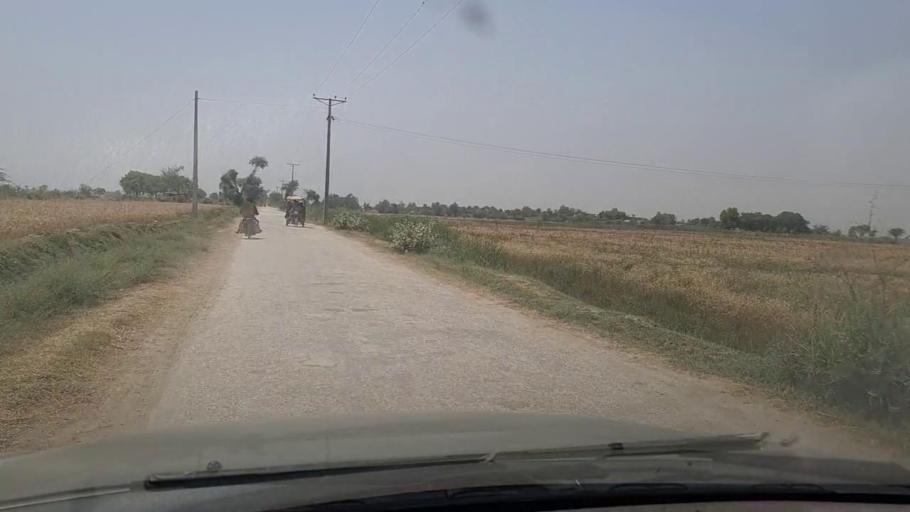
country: PK
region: Sindh
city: Miro Khan
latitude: 27.7634
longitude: 68.1235
